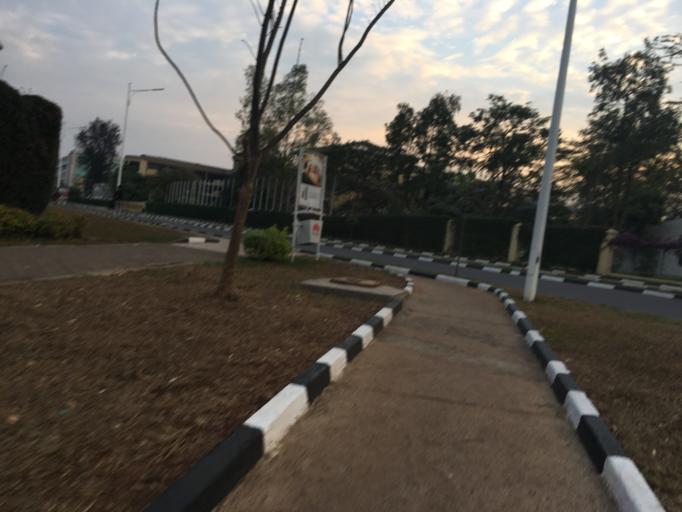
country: RW
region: Kigali
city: Kigali
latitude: -1.9576
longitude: 30.0622
